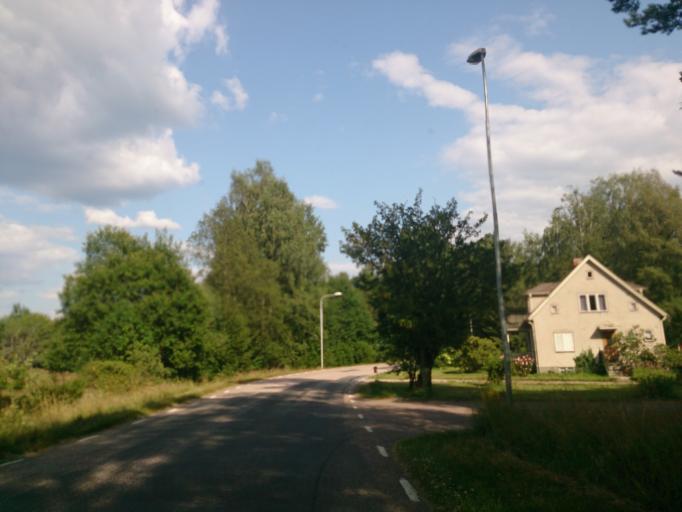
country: SE
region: Joenkoeping
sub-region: Varnamo Kommun
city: Bredaryd
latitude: 57.0904
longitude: 13.6873
